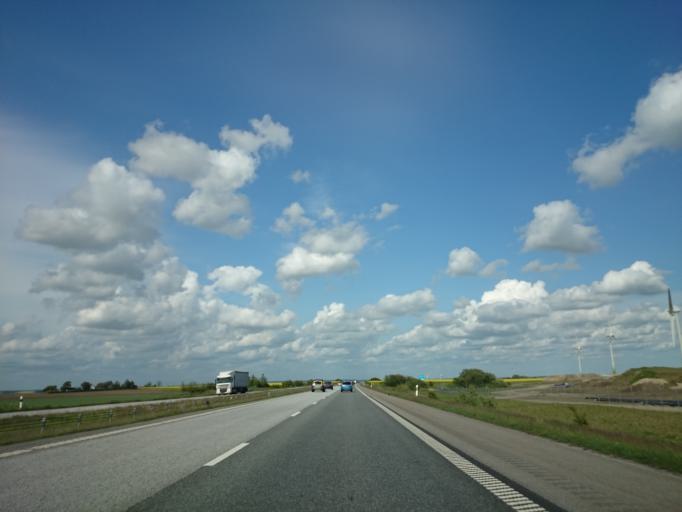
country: SE
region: Skane
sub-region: Lunds Kommun
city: Lund
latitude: 55.7369
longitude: 13.2445
